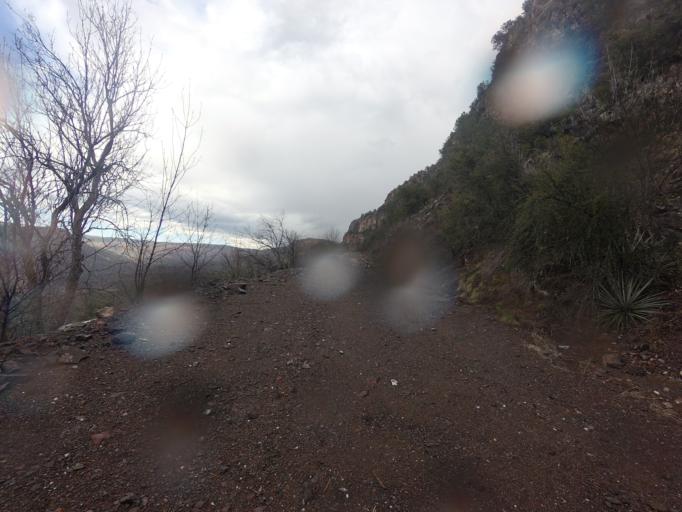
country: US
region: Arizona
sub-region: Gila County
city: Pine
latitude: 34.4078
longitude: -111.5858
